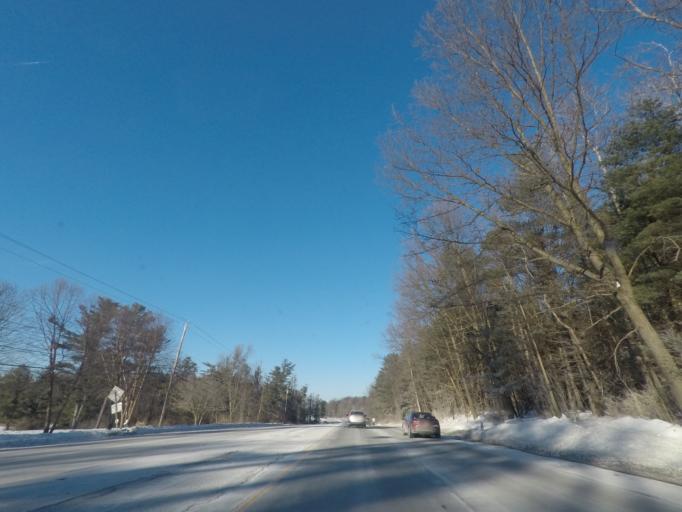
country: US
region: New York
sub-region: Saratoga County
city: Saratoga Springs
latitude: 43.0470
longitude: -73.7893
